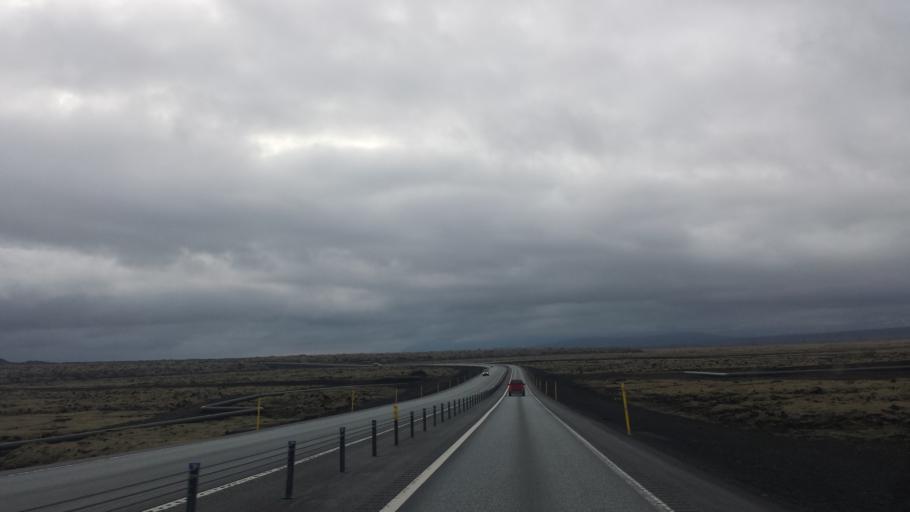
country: IS
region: South
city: THorlakshoefn
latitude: 64.0242
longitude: -21.4160
